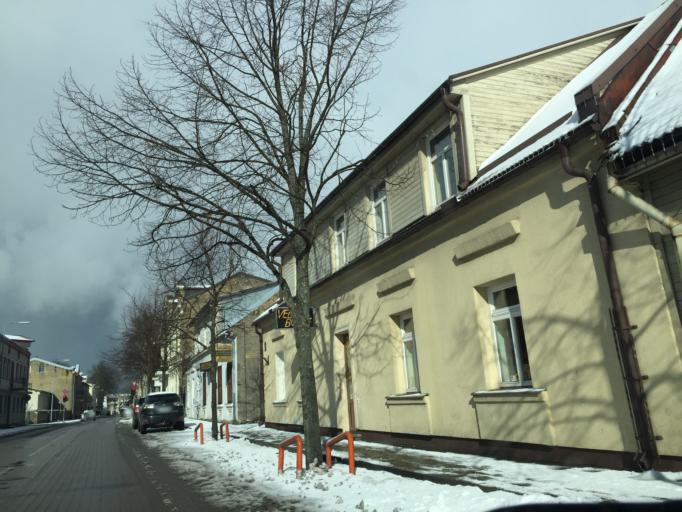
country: LV
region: Ventspils
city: Ventspils
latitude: 57.3911
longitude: 21.5596
